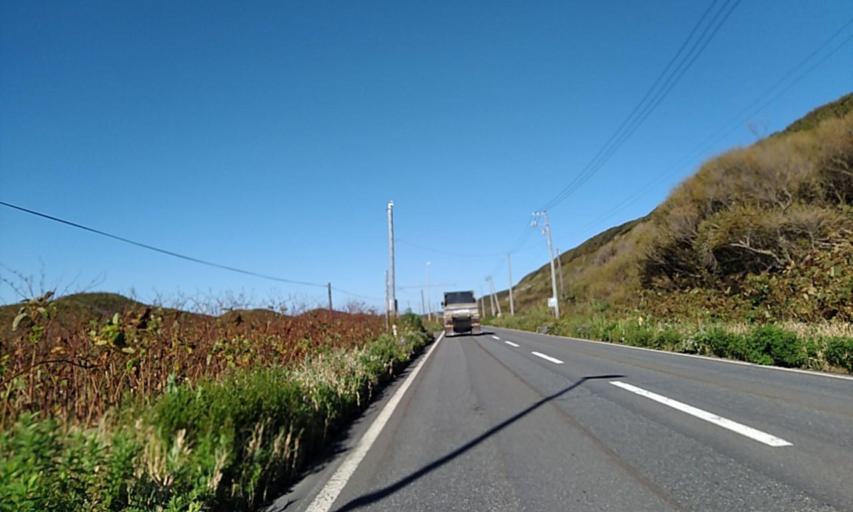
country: JP
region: Hokkaido
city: Shizunai-furukawacho
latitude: 42.4660
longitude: 142.1463
